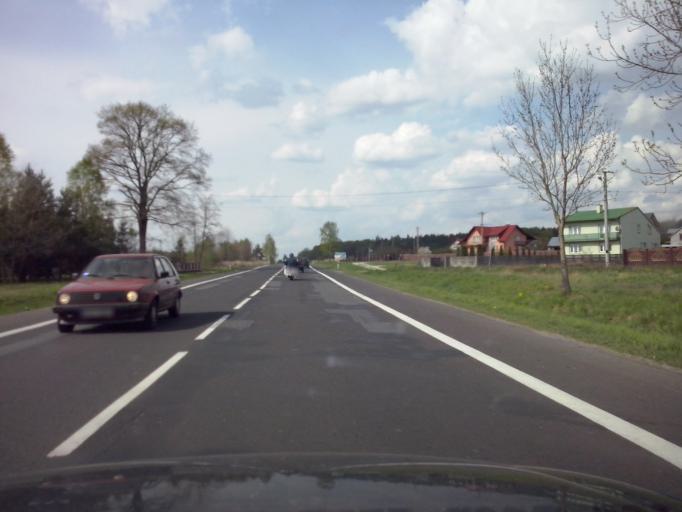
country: PL
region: Subcarpathian Voivodeship
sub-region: Powiat rzeszowski
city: Gorno
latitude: 50.2904
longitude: 22.1337
